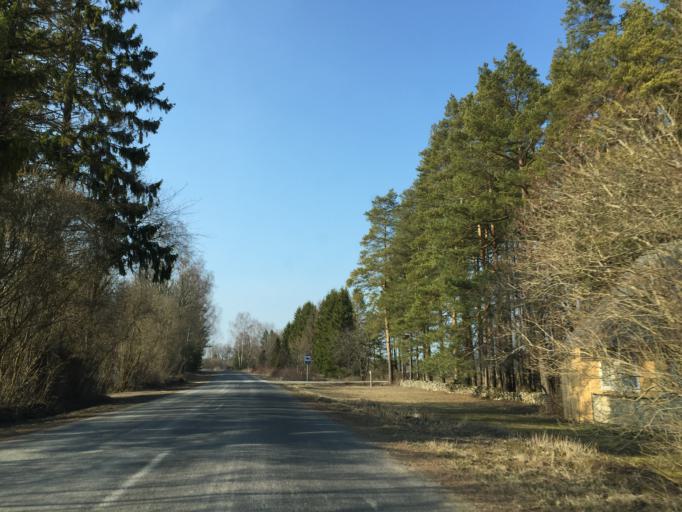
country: EE
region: Saare
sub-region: Orissaare vald
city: Orissaare
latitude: 58.6046
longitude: 23.3144
